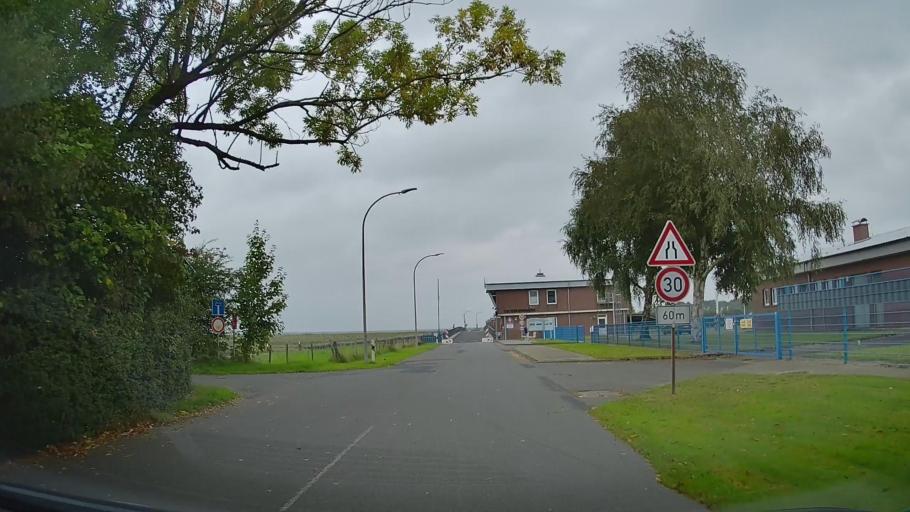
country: DE
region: Lower Saxony
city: Neuhaus an der Oste
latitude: 53.8199
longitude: 9.0380
